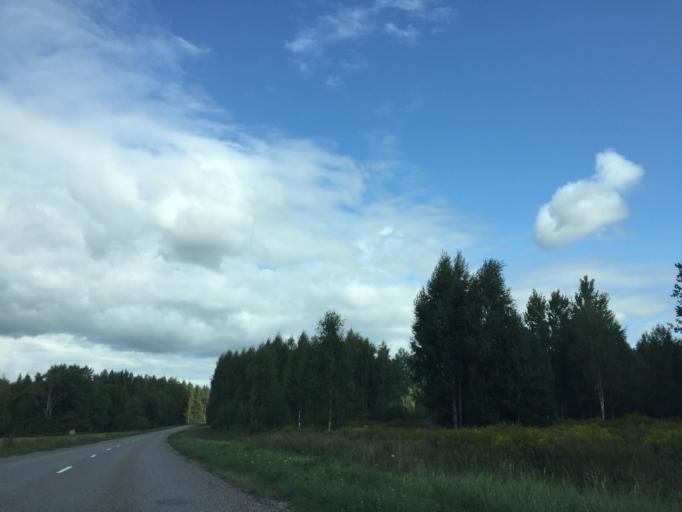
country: LV
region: Pargaujas
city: Stalbe
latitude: 57.4290
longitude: 24.9258
